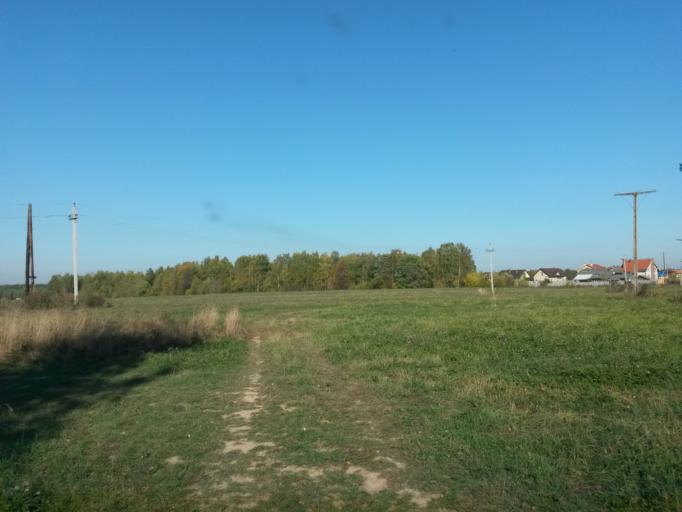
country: RU
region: Moskovskaya
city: Lyubuchany
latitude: 55.2608
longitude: 37.6229
